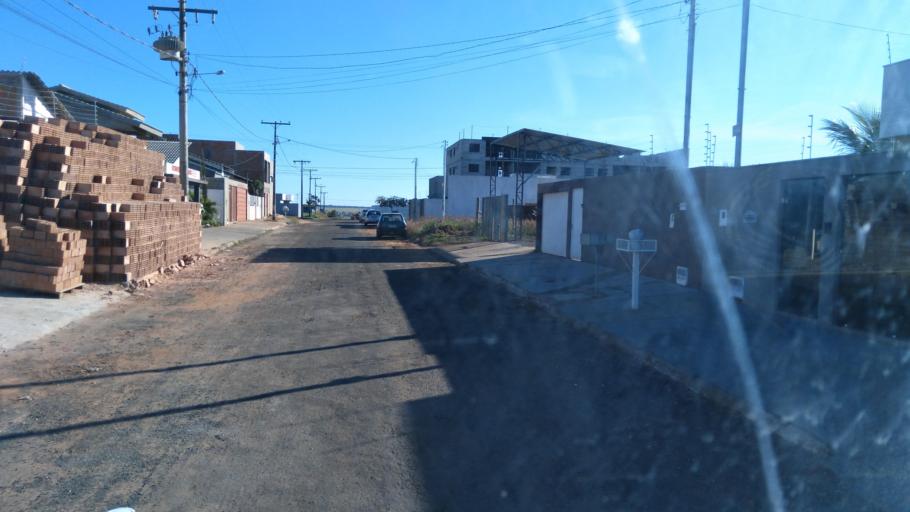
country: BR
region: Goias
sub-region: Mineiros
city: Mineiros
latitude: -17.5457
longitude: -52.5515
